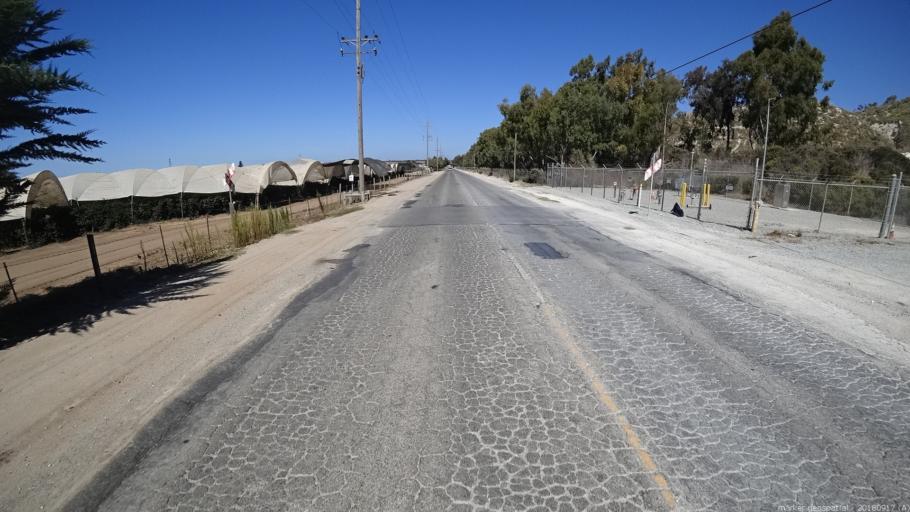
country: US
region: California
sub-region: Monterey County
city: Prunedale
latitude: 36.7503
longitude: -121.6072
